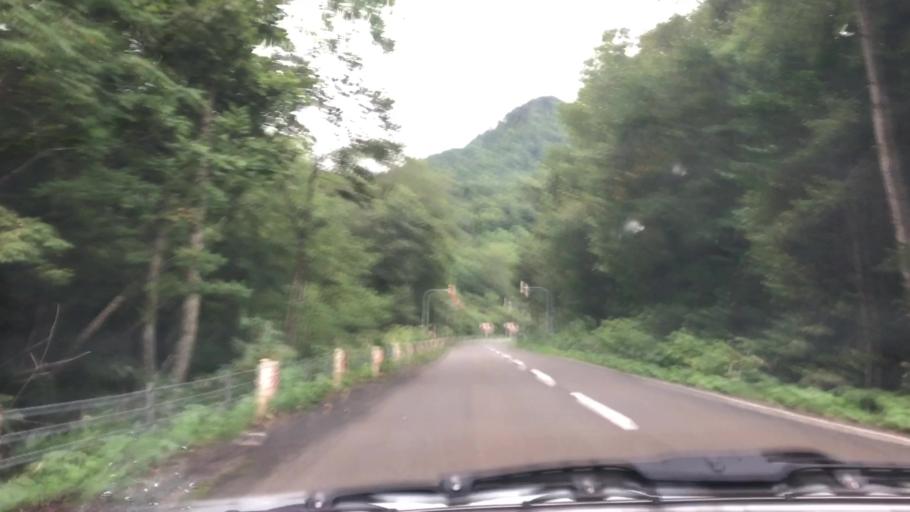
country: JP
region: Hokkaido
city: Shimo-furano
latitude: 42.9169
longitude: 142.3741
